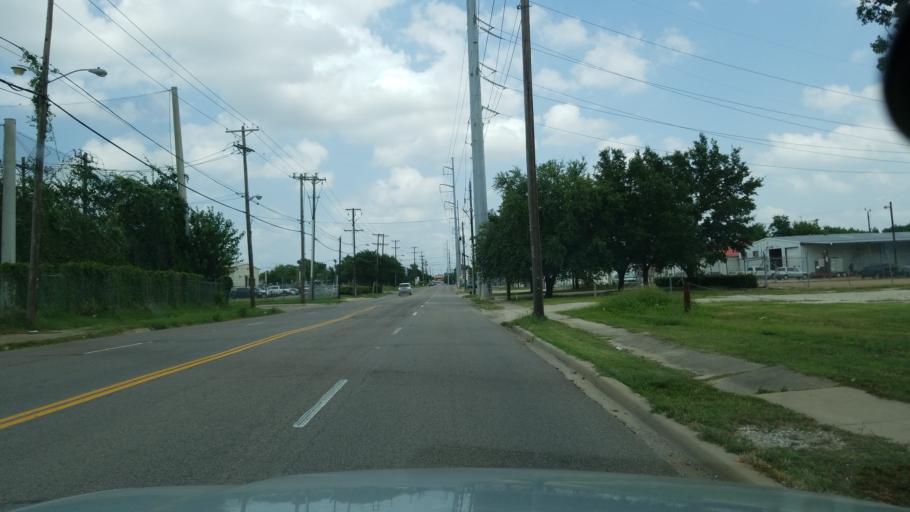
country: US
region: Texas
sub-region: Dallas County
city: University Park
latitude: 32.8265
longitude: -96.8629
